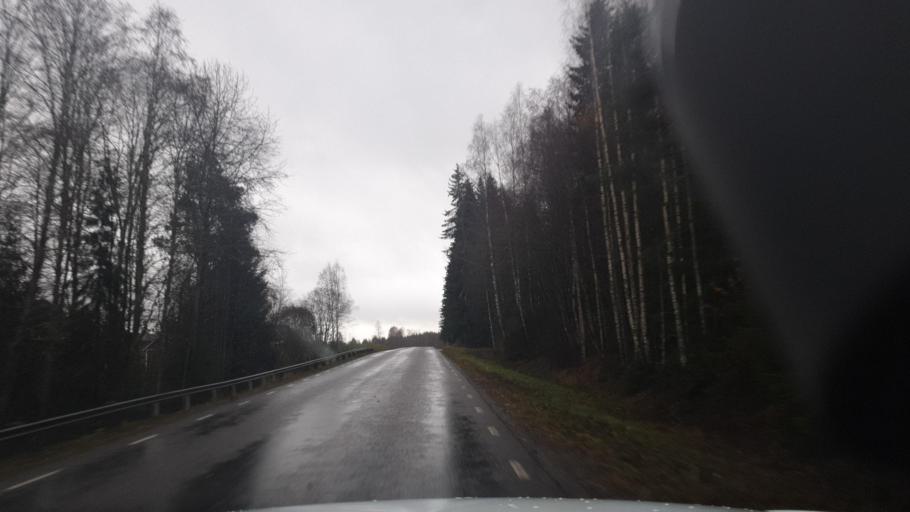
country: SE
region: Vaermland
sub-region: Eda Kommun
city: Charlottenberg
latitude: 59.7984
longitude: 12.1542
